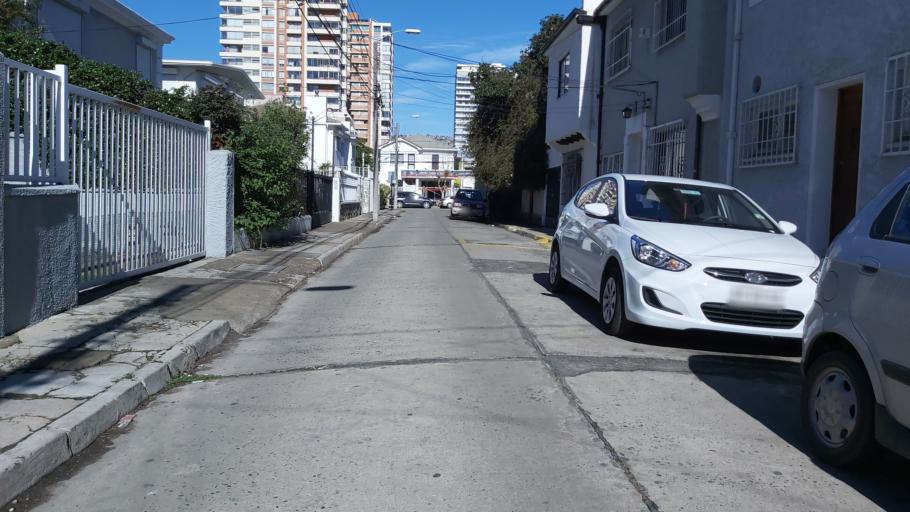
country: CL
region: Valparaiso
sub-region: Provincia de Valparaiso
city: Vina del Mar
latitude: -33.0169
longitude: -71.5561
